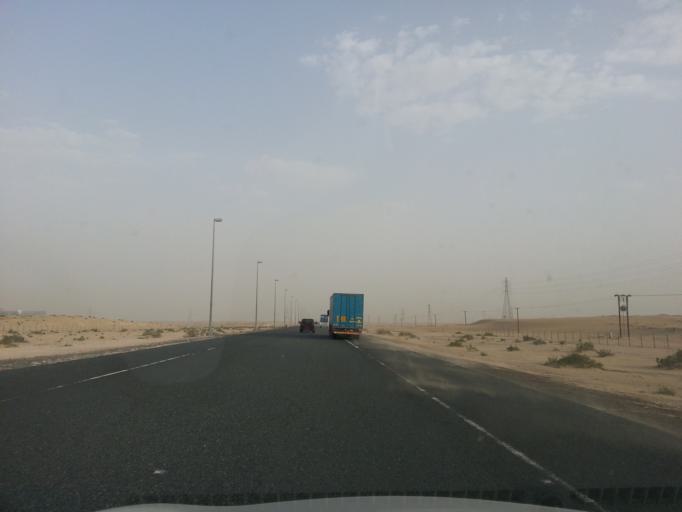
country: AE
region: Dubai
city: Dubai
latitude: 24.7489
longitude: 55.1060
